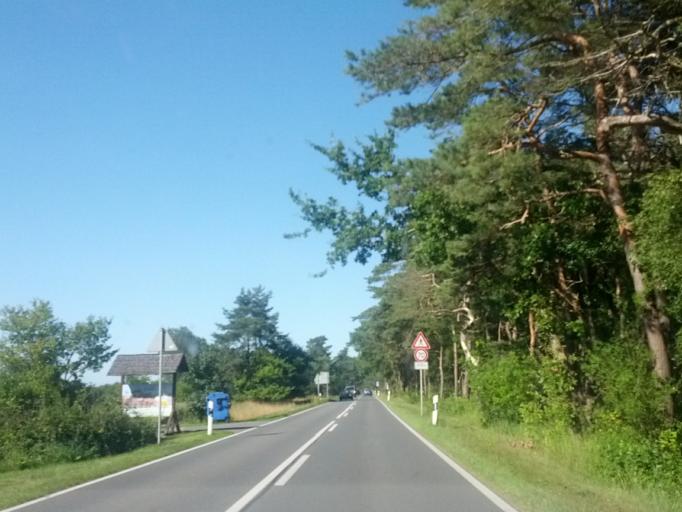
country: DE
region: Mecklenburg-Vorpommern
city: Ostseebad Gohren
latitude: 54.3032
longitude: 13.7145
